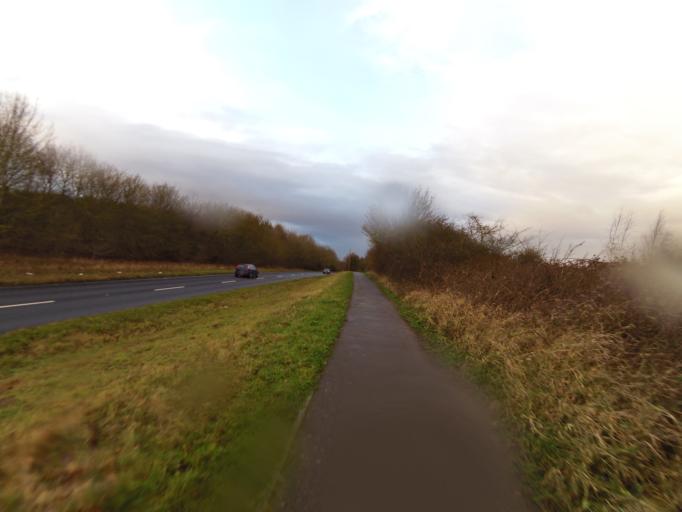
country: GB
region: England
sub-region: Suffolk
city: Needham Market
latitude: 52.1666
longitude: 1.0319
